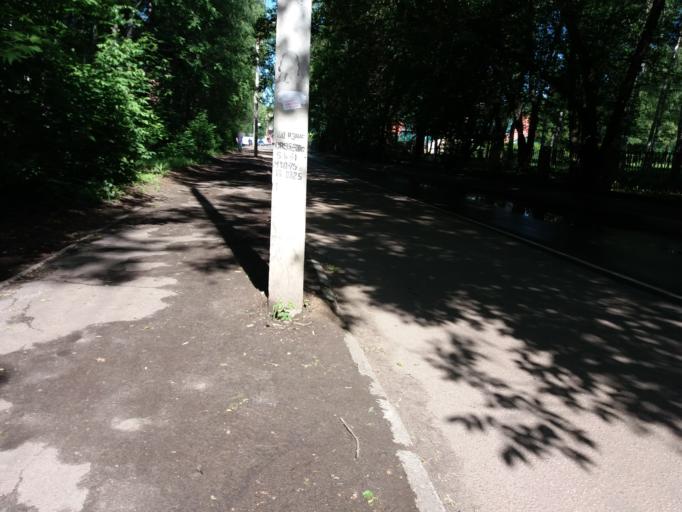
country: RU
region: Jaroslavl
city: Yaroslavl
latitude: 57.6364
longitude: 39.8516
